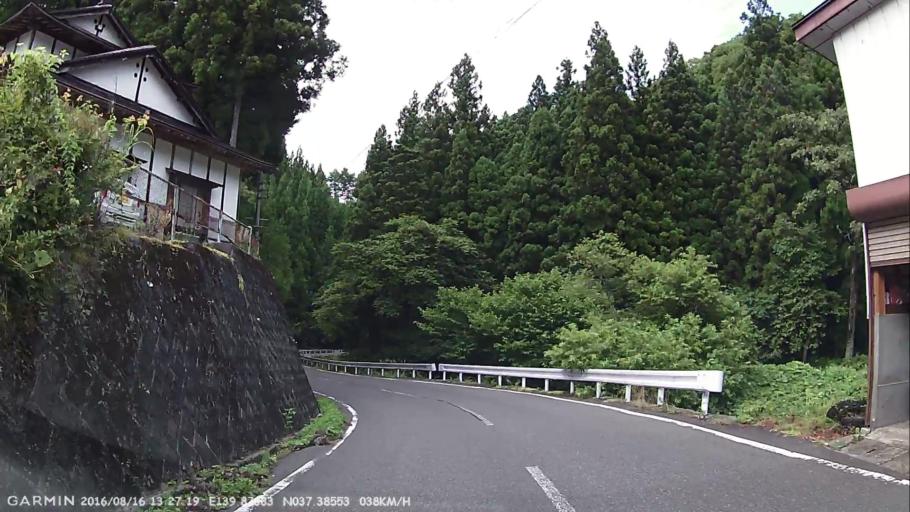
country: JP
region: Fukushima
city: Kitakata
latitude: 37.3856
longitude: 139.8708
